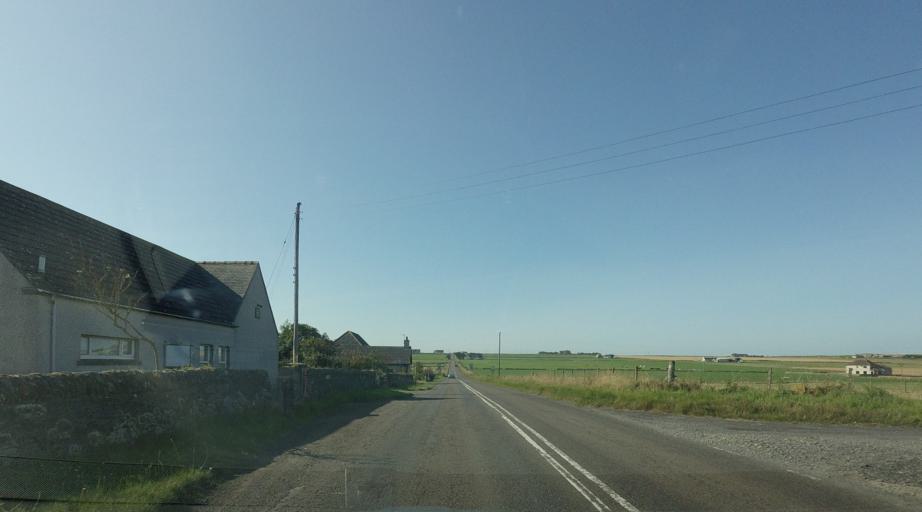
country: GB
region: Scotland
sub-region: Highland
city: Thurso
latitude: 58.5936
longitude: -3.4551
